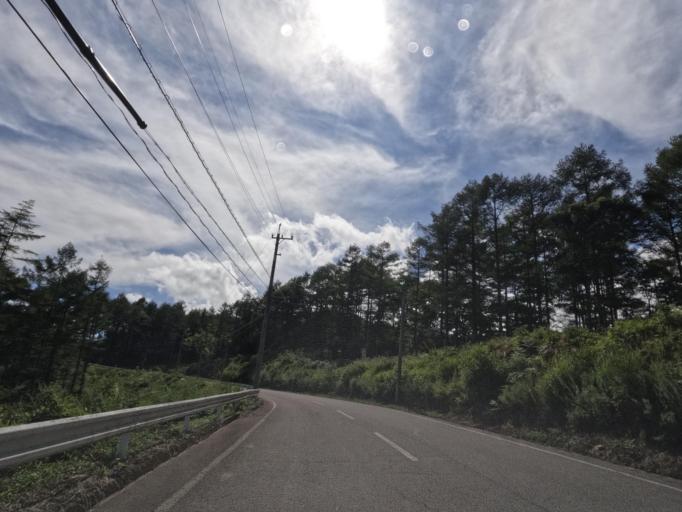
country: JP
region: Yamanashi
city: Nirasaki
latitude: 35.9355
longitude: 138.4624
